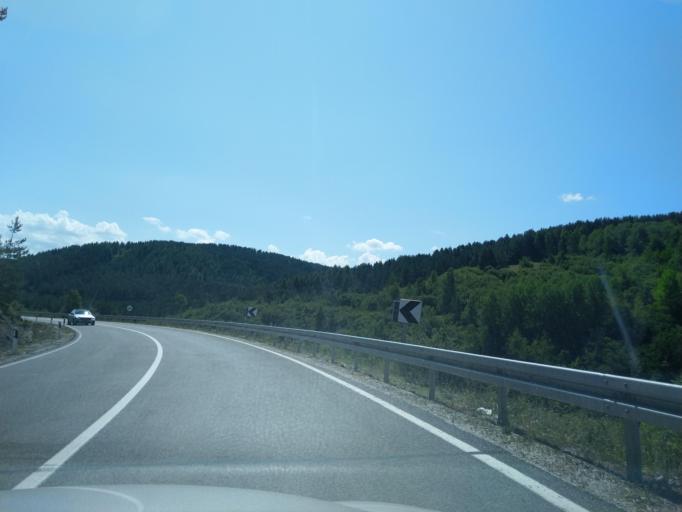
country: RS
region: Central Serbia
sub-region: Zlatiborski Okrug
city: Sjenica
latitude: 43.2838
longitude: 19.9472
